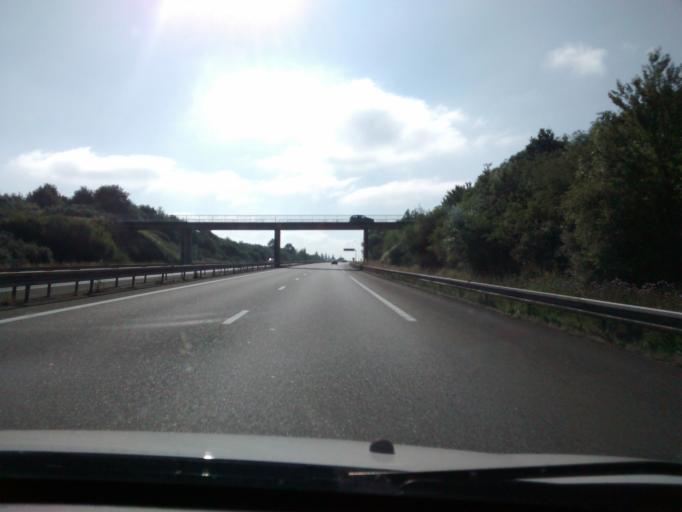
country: FR
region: Pays de la Loire
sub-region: Departement de la Mayenne
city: Bonchamp-les-Laval
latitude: 48.0983
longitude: -0.7066
